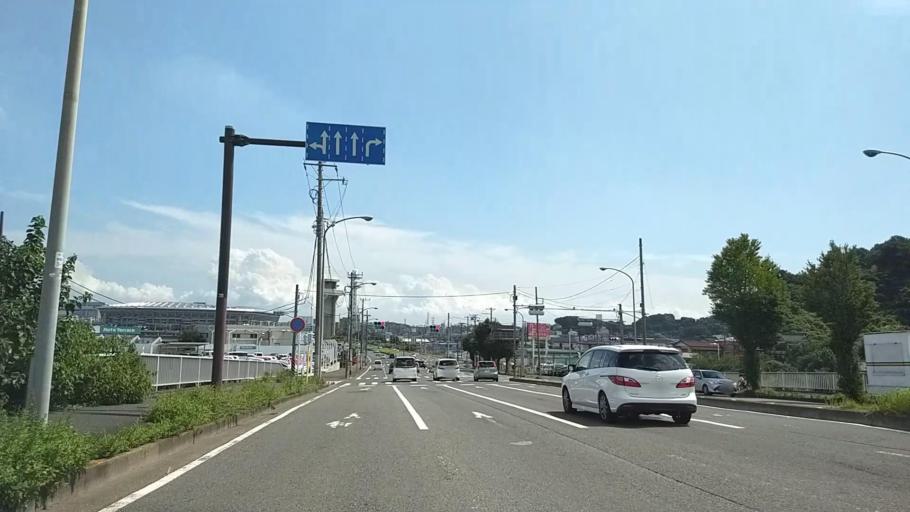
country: JP
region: Kanagawa
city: Yokohama
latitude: 35.5159
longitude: 139.5951
